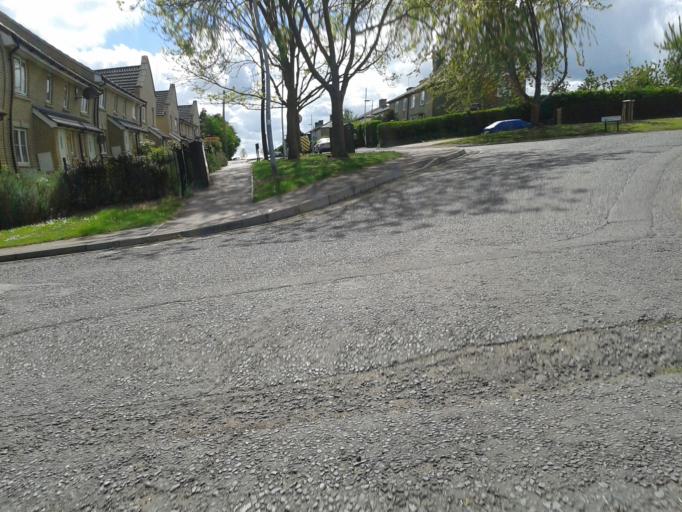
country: GB
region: England
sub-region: Cambridgeshire
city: Cambridge
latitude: 52.2146
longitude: 0.1471
